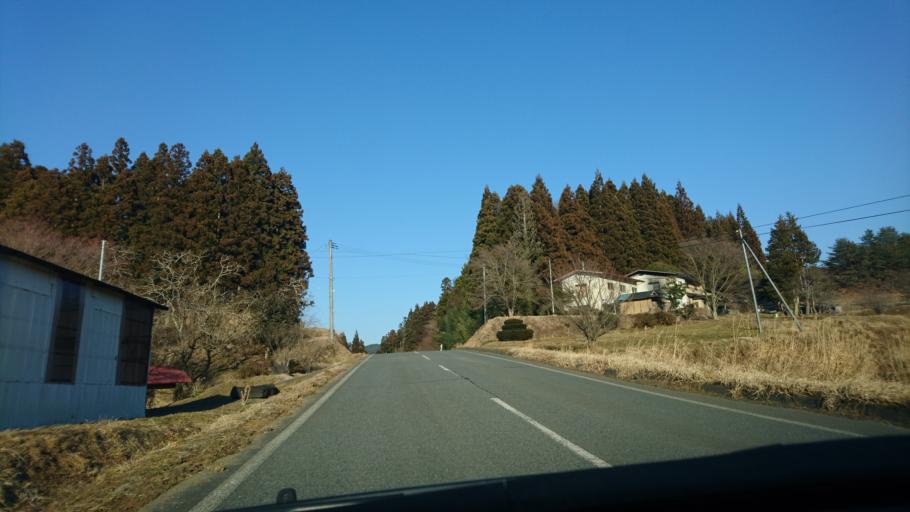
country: JP
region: Iwate
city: Ichinoseki
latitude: 38.8379
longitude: 141.3766
